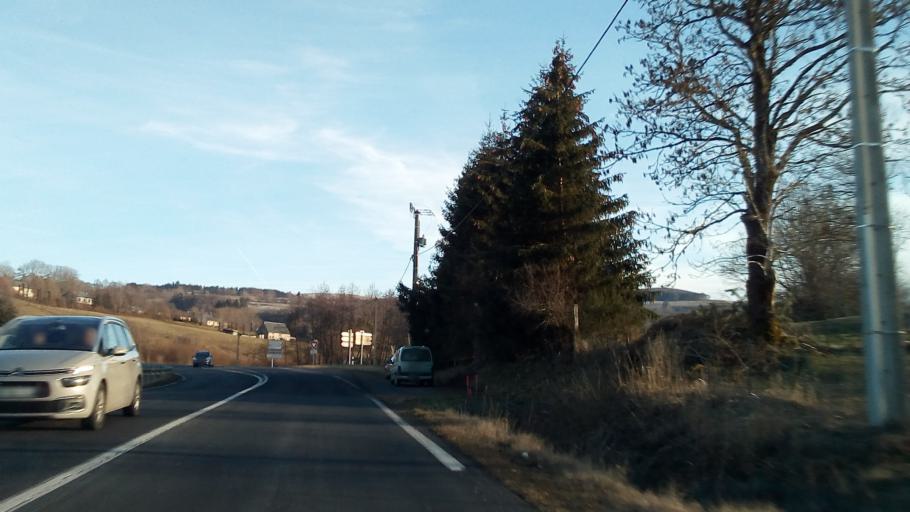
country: FR
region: Auvergne
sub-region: Departement du Puy-de-Dome
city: La Bourboule
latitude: 45.6422
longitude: 2.7230
